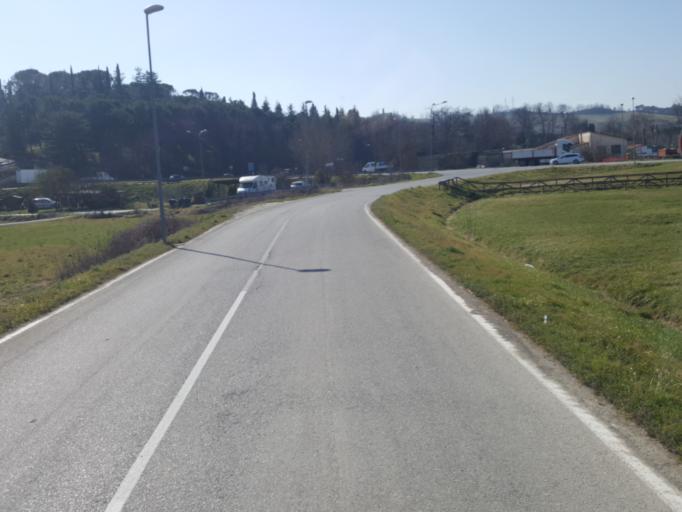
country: IT
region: Tuscany
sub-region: Province of Arezzo
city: Terranuova Bracciolini
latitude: 43.5487
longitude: 11.5891
